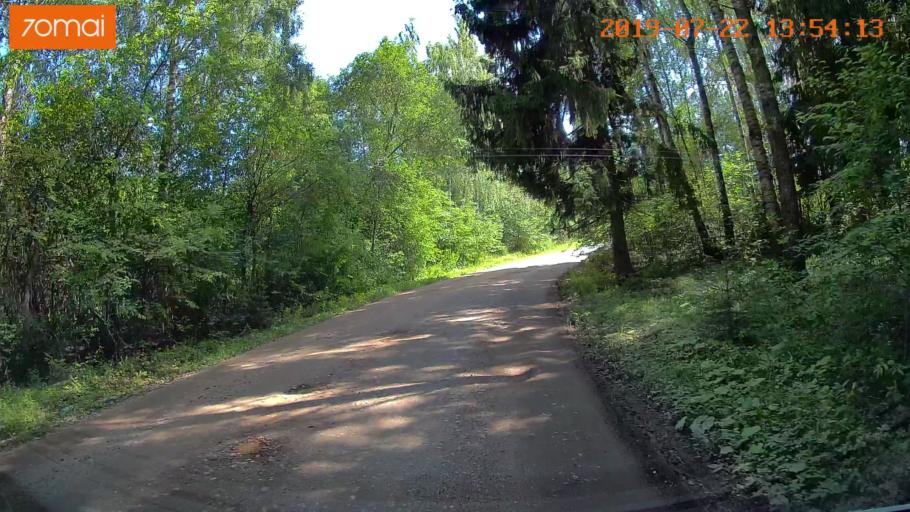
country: RU
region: Ivanovo
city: Novo-Talitsy
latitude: 57.0790
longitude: 40.8799
